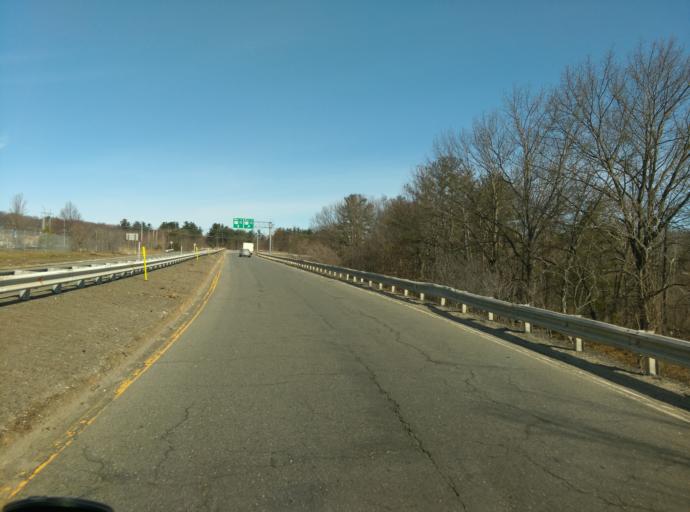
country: US
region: Massachusetts
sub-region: Essex County
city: Lawrence
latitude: 42.7440
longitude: -71.1543
